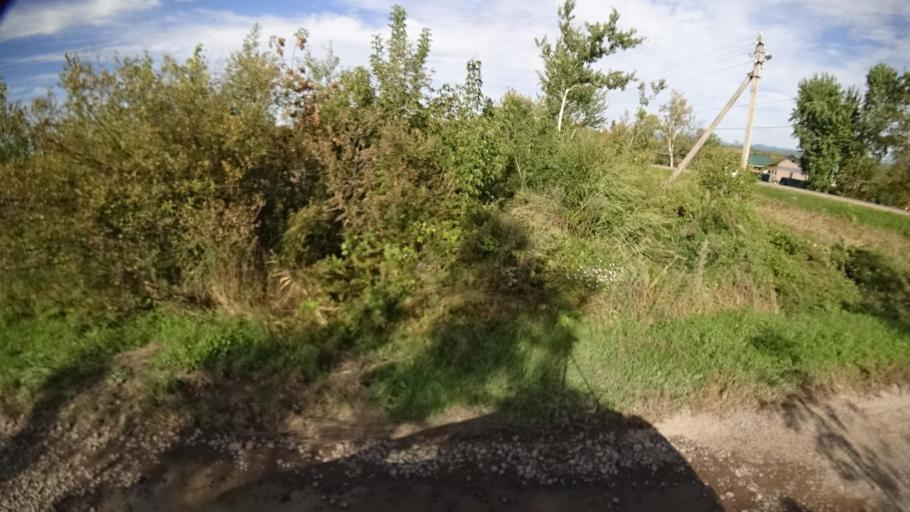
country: RU
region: Primorskiy
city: Dostoyevka
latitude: 44.3070
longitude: 133.4507
